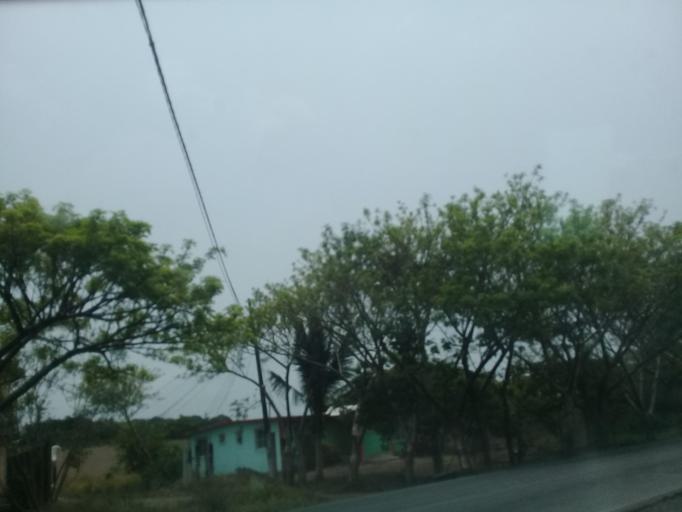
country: MX
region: Veracruz
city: El Tejar
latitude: 19.0464
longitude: -96.1902
